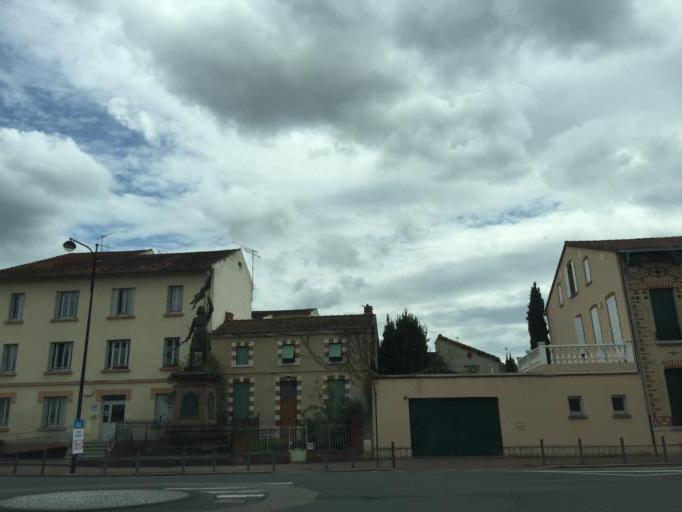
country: FR
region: Midi-Pyrenees
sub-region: Departement du Tarn
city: Albi
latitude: 43.9225
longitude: 2.1417
